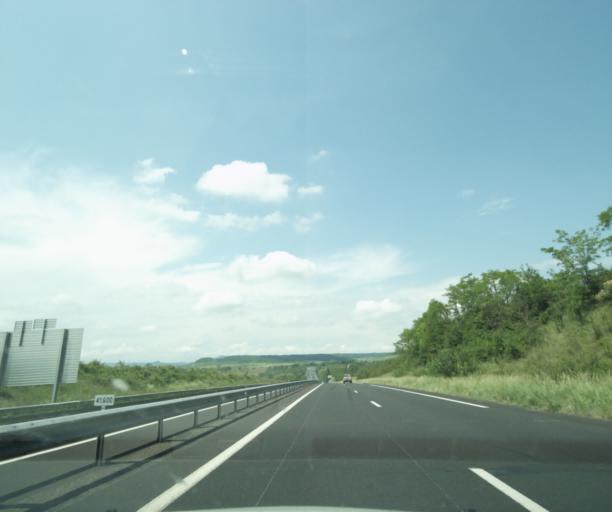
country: FR
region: Auvergne
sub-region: Departement du Puy-de-Dome
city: Le Breuil-sur-Couze
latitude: 45.4579
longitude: 3.2614
